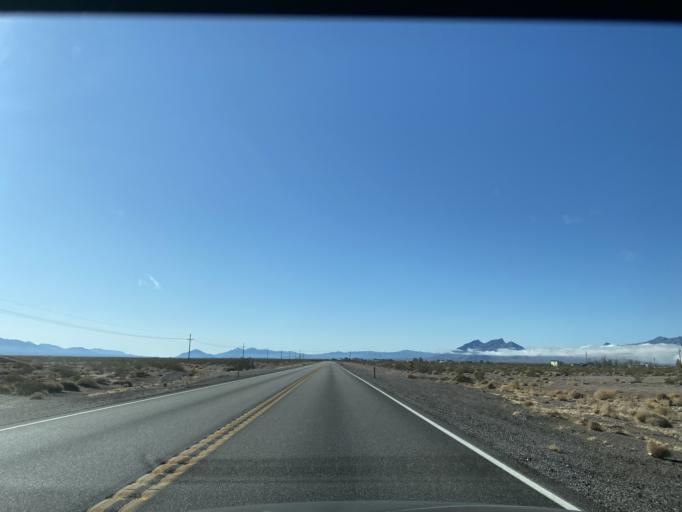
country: US
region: Nevada
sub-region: Nye County
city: Beatty
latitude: 36.5143
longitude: -116.4203
